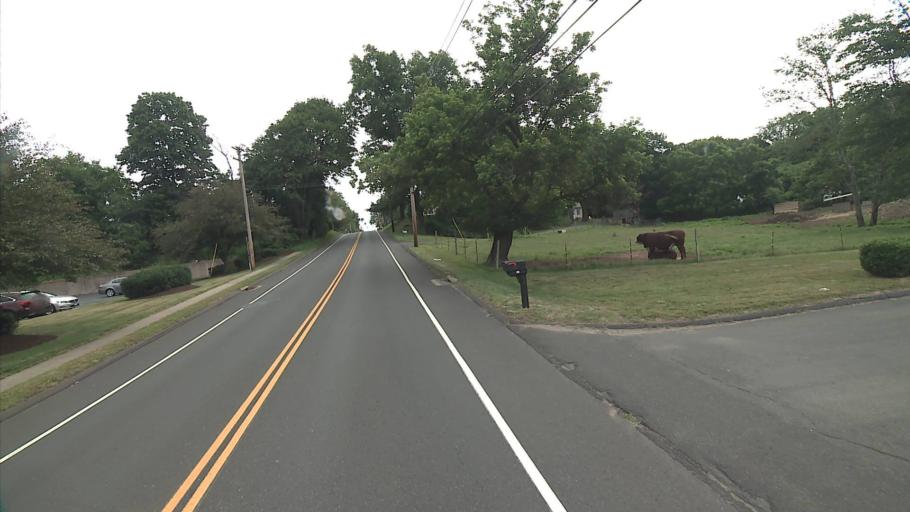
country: US
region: Connecticut
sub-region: New Haven County
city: Wallingford
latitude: 41.4856
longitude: -72.8230
